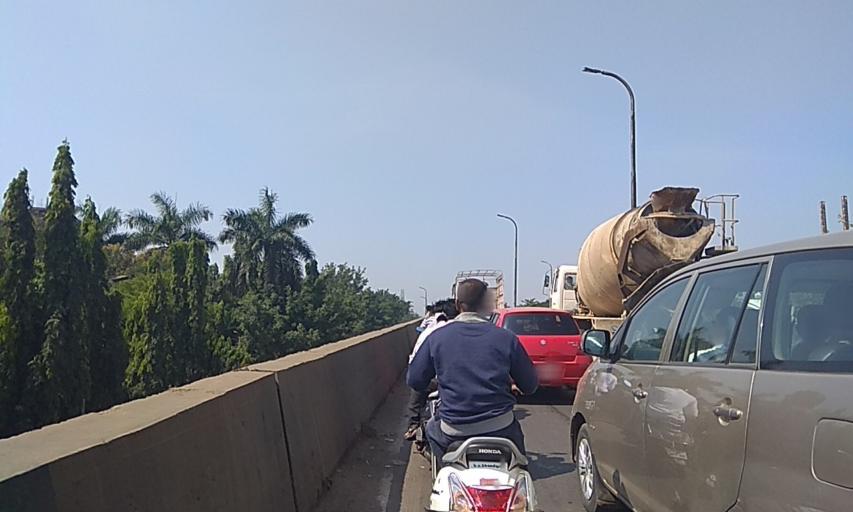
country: IN
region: Maharashtra
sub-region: Pune Division
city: Pune
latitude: 18.5021
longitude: 73.9284
